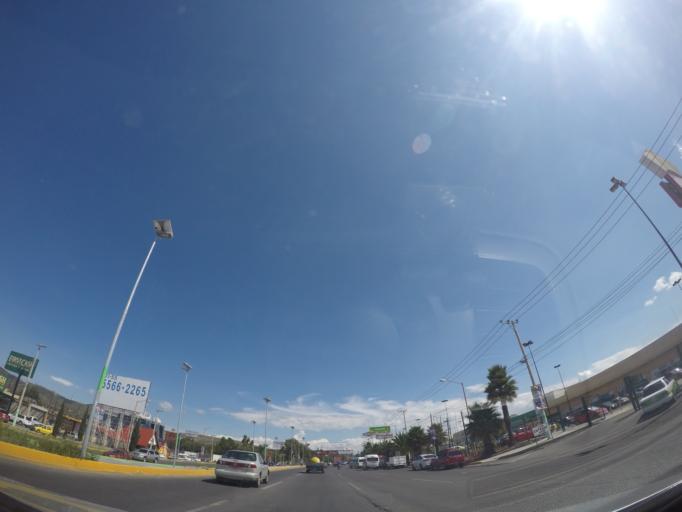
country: MX
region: Hidalgo
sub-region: Mineral de la Reforma
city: Unidad Minera 11 de Julio
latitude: 20.0978
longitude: -98.7161
